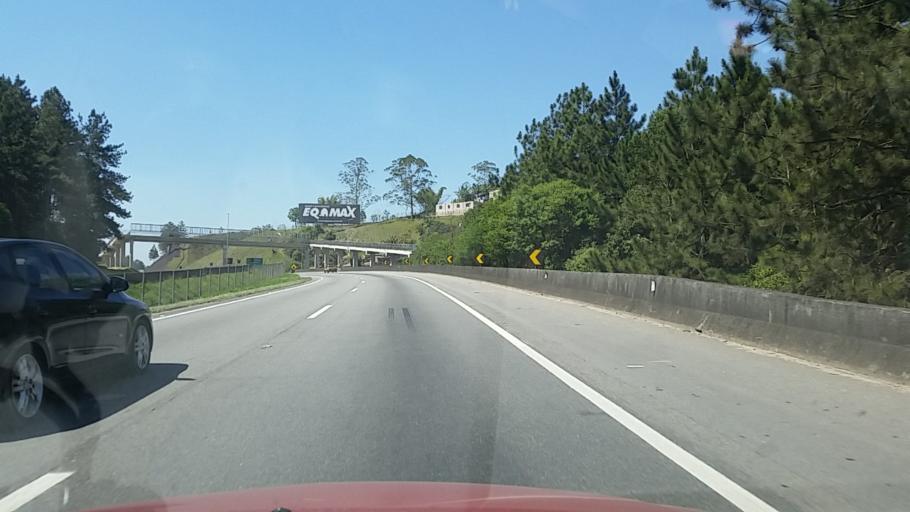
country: BR
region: Sao Paulo
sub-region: Juquitiba
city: Juquitiba
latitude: -23.9382
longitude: -47.0840
